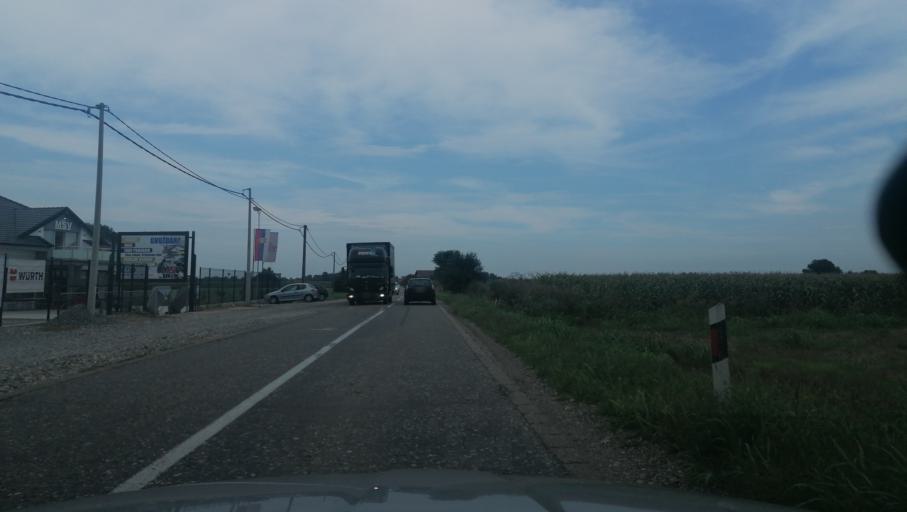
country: RS
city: Klenje
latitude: 44.8242
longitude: 19.4553
